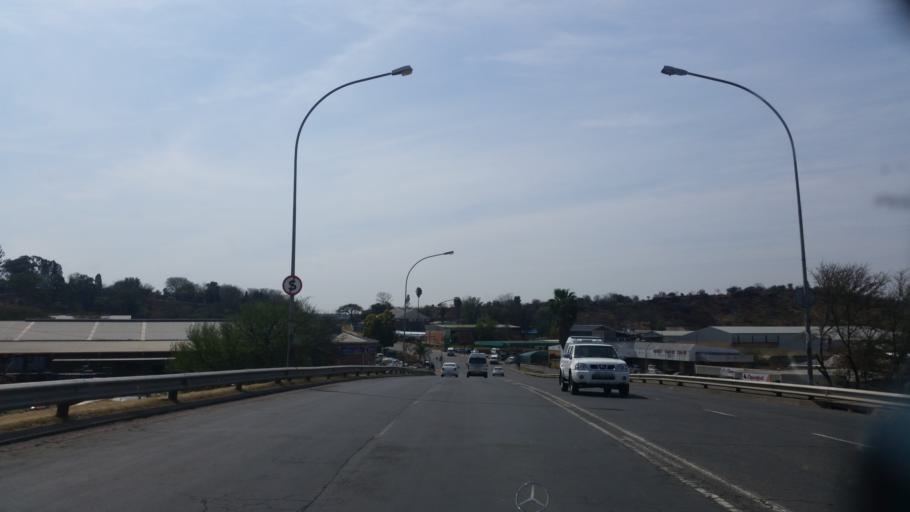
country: ZA
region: KwaZulu-Natal
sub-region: uThukela District Municipality
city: Ladysmith
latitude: -28.5524
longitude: 29.7882
